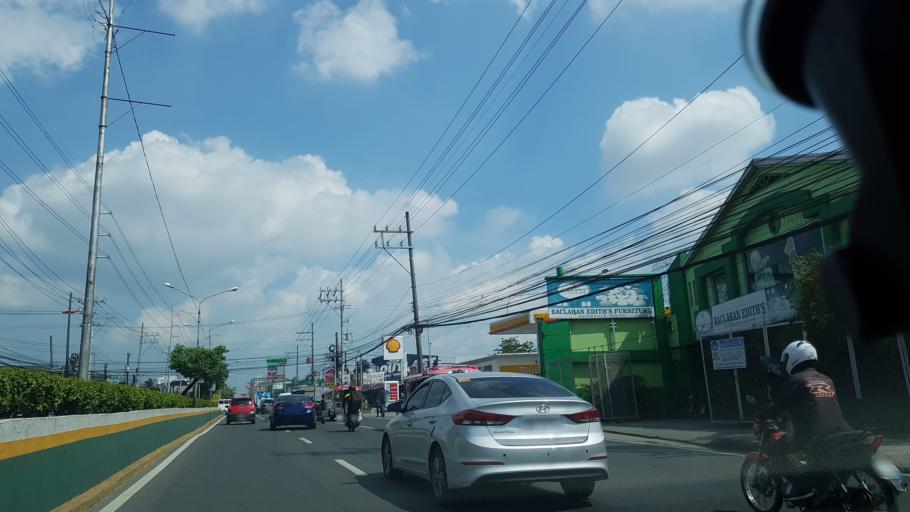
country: PH
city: Sambayanihan People's Village
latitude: 14.4679
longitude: 121.0133
